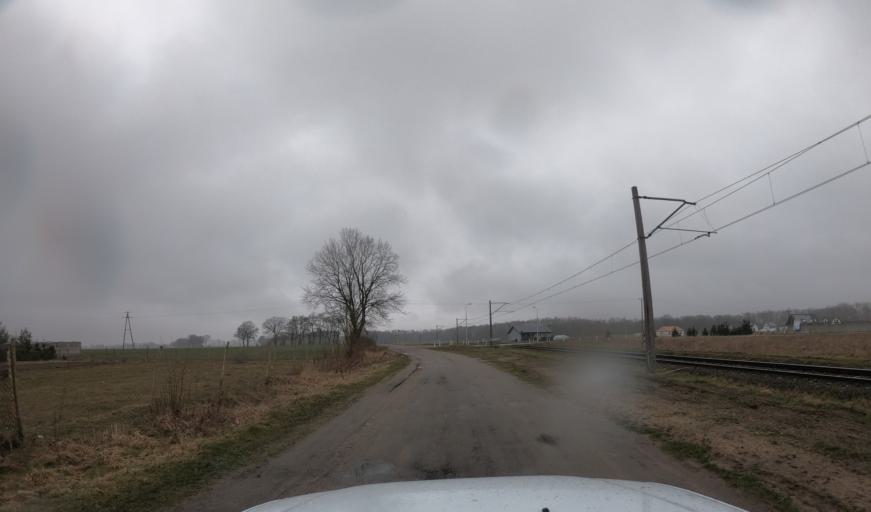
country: PL
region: West Pomeranian Voivodeship
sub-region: Powiat kamienski
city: Kamien Pomorski
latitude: 53.9017
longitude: 14.8238
